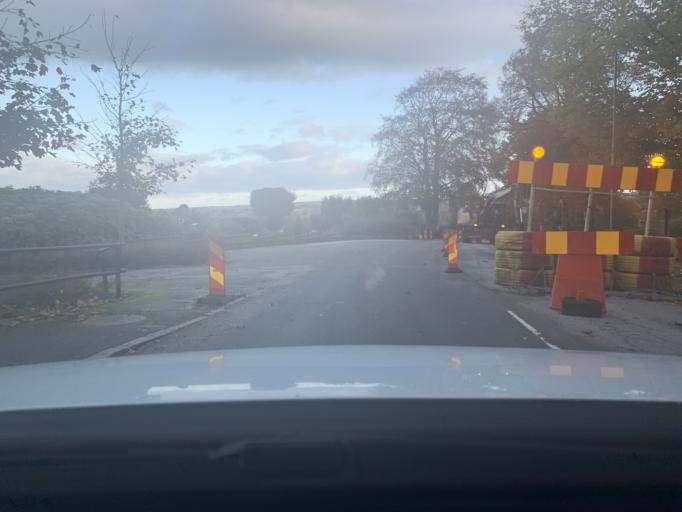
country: SE
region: Skane
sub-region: Horby Kommun
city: Hoerby
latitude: 55.8437
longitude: 13.6547
